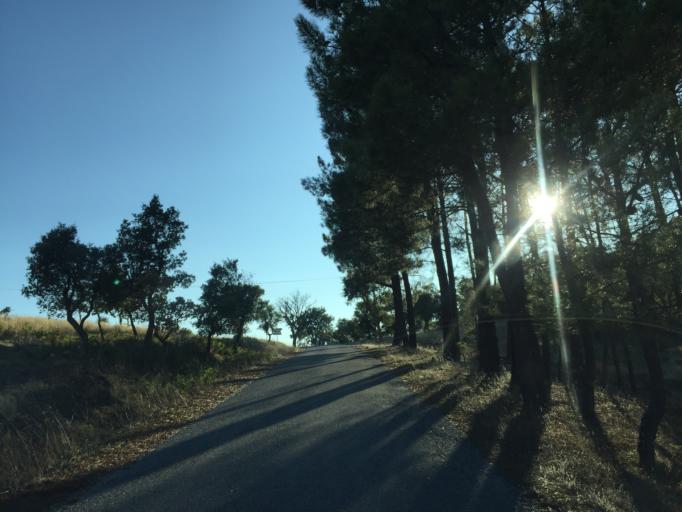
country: PT
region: Portalegre
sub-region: Castelo de Vide
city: Castelo de Vide
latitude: 39.4003
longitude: -7.4486
